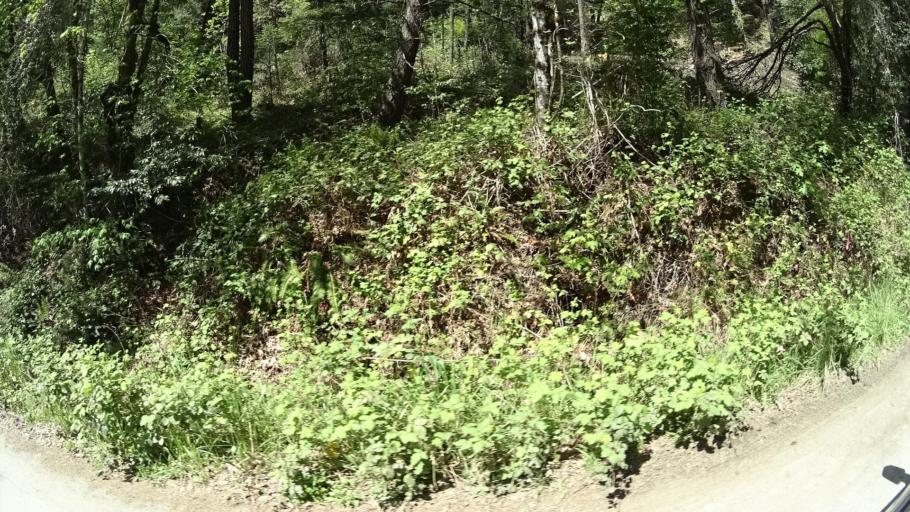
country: US
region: California
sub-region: Humboldt County
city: Redway
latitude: 40.1994
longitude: -123.5260
